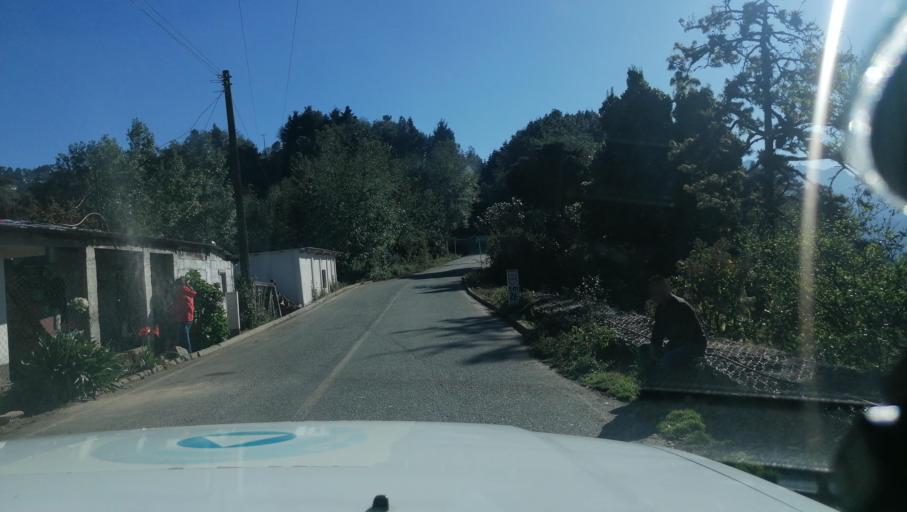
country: MX
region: Chiapas
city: Motozintla de Mendoza
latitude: 15.2538
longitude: -92.2179
